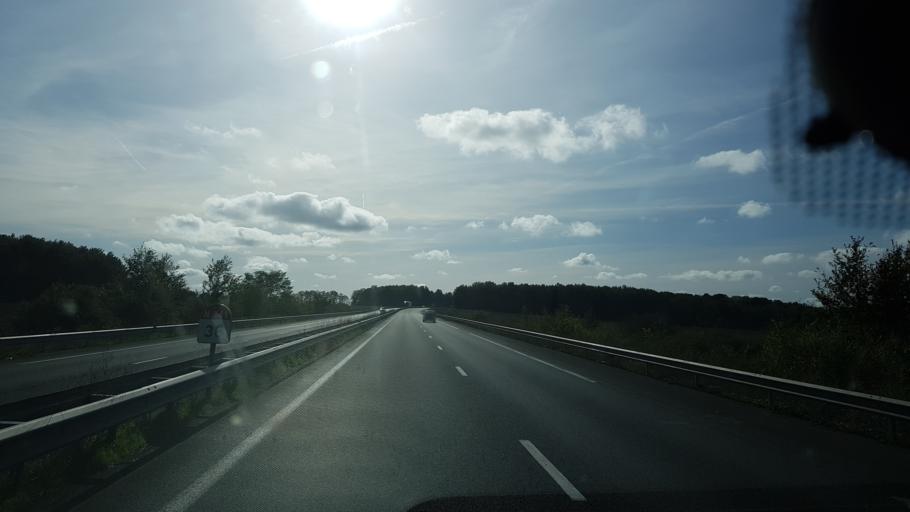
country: FR
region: Poitou-Charentes
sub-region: Departement de la Charente
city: Chasseneuil-sur-Bonnieure
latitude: 45.7986
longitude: 0.4358
